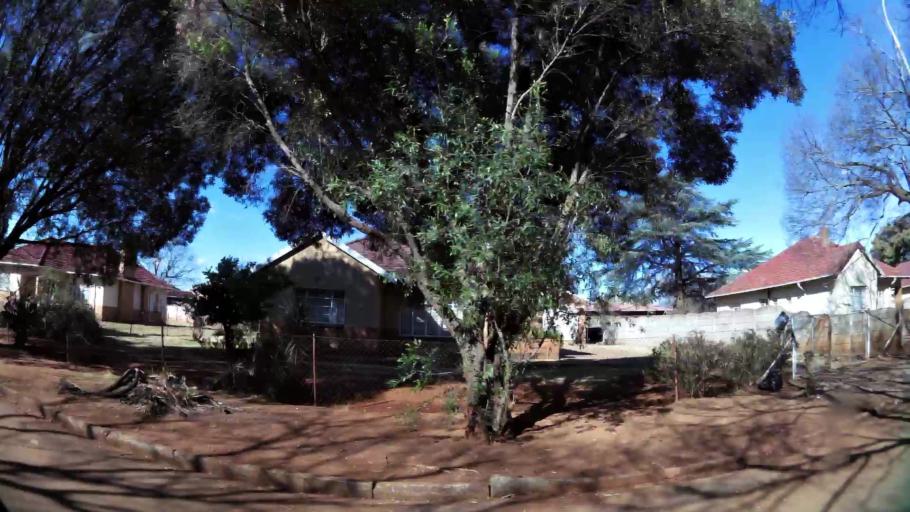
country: ZA
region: Gauteng
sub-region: West Rand District Municipality
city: Carletonville
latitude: -26.3611
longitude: 27.3968
